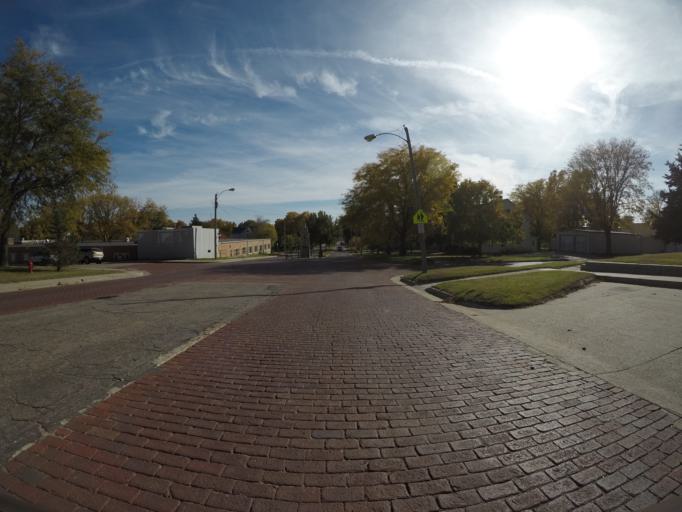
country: US
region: Kansas
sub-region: Decatur County
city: Oberlin
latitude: 39.8245
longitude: -100.5291
